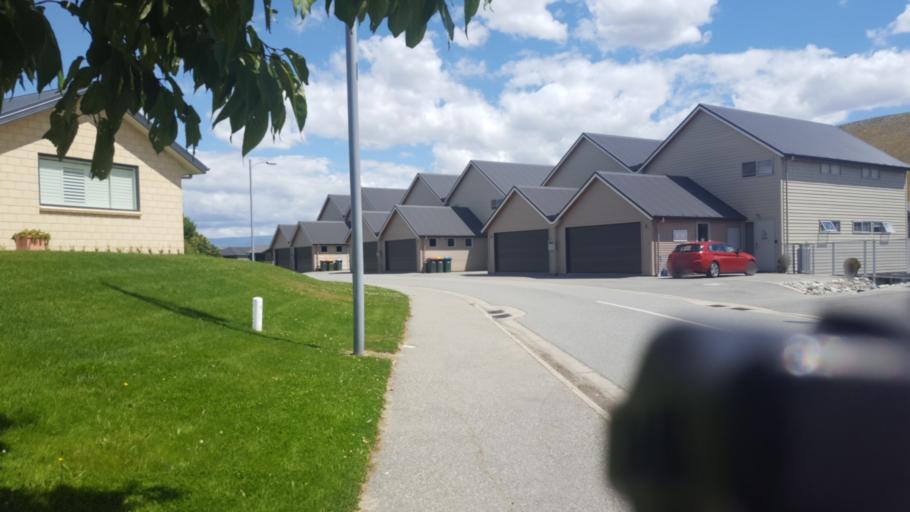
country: NZ
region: Otago
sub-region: Queenstown-Lakes District
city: Wanaka
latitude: -44.9800
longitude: 169.2376
